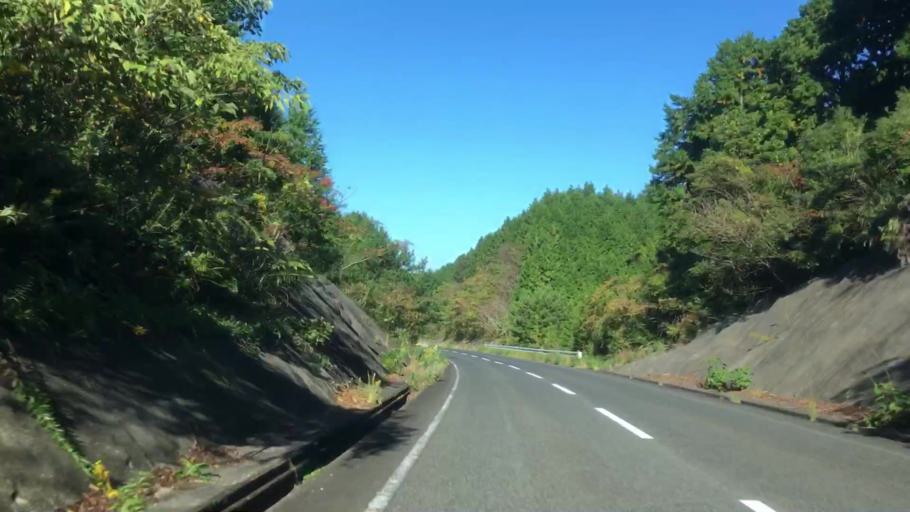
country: JP
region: Nagasaki
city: Sasebo
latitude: 33.0262
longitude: 129.6955
